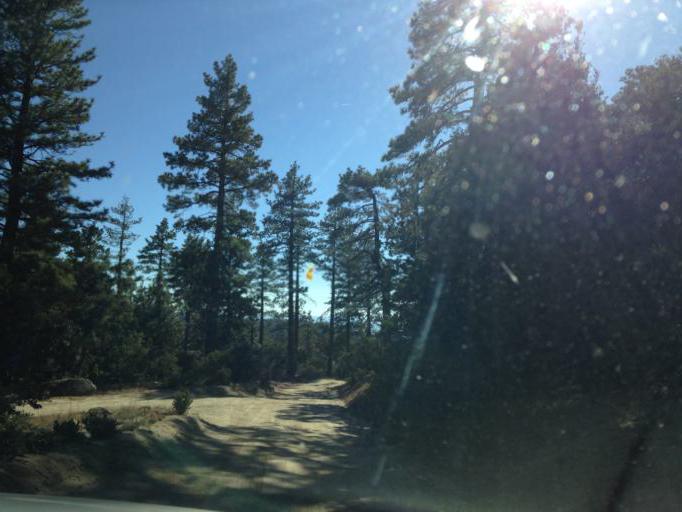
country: US
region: California
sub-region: Riverside County
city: Idyllwild-Pine Cove
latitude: 33.8102
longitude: -116.7491
